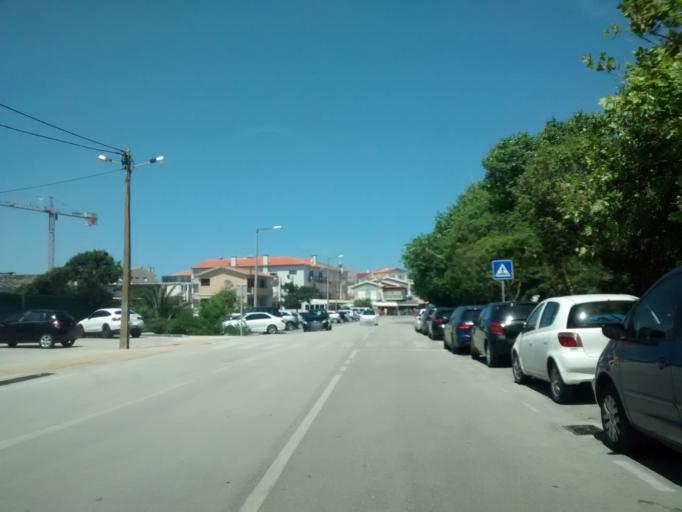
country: PT
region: Coimbra
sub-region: Mira
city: Mira
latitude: 40.4506
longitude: -8.8015
